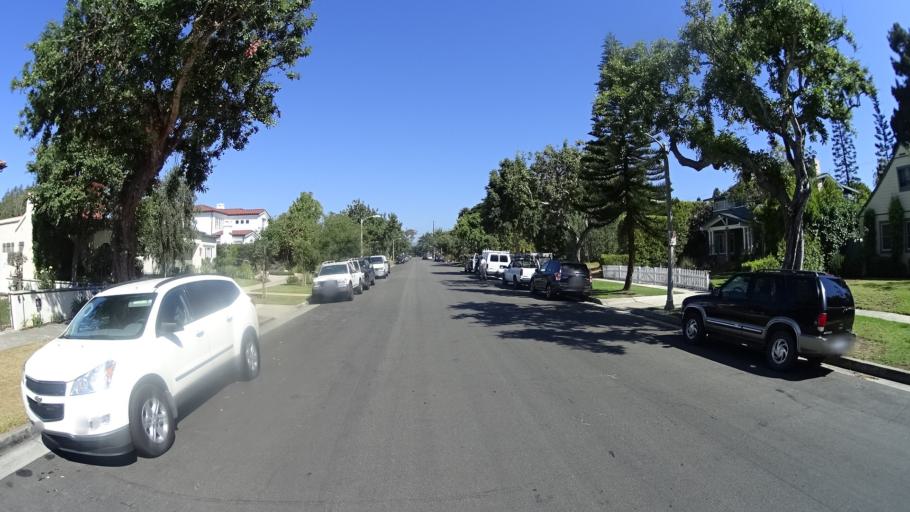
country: US
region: California
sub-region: Los Angeles County
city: Santa Monica
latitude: 34.0310
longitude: -118.5049
